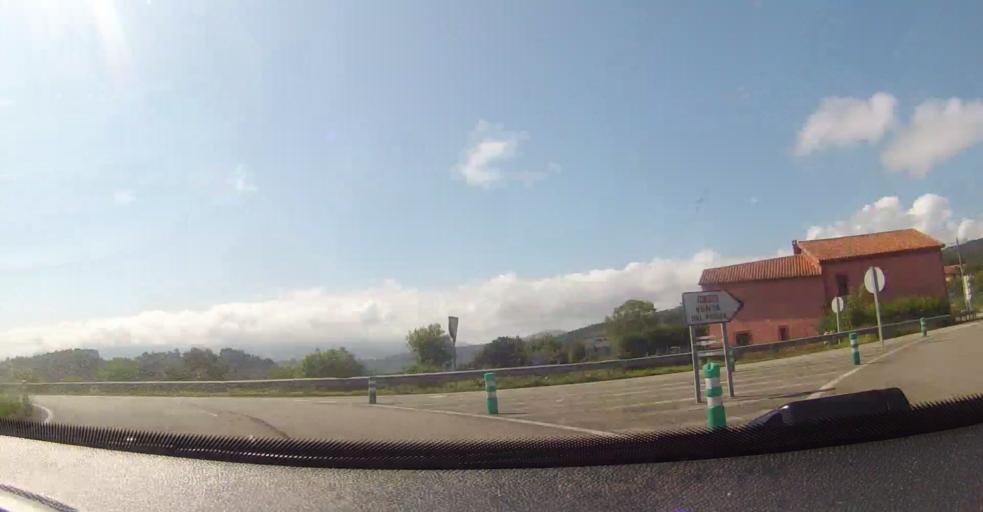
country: ES
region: Asturias
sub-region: Province of Asturias
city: Colunga
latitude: 43.5031
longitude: -5.3327
